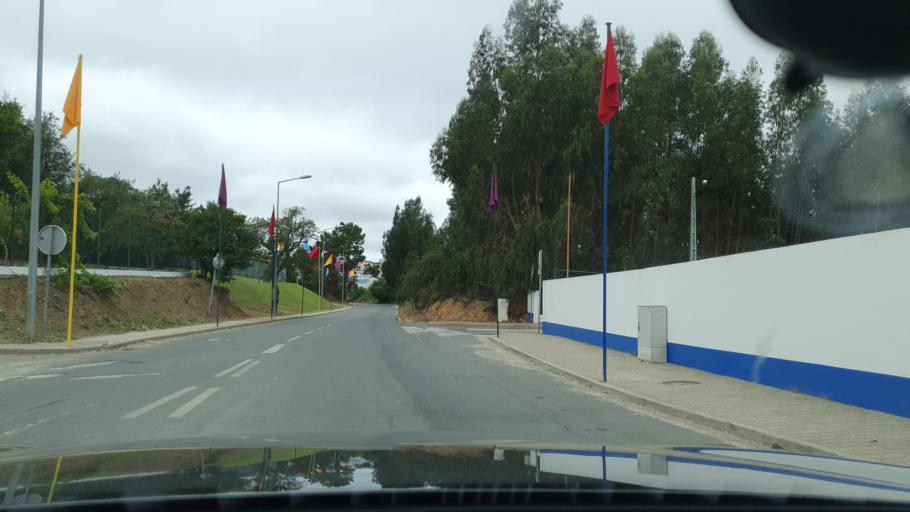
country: PT
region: Beja
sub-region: Odemira
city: Sao Teotonio
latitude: 37.5091
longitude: -8.7105
